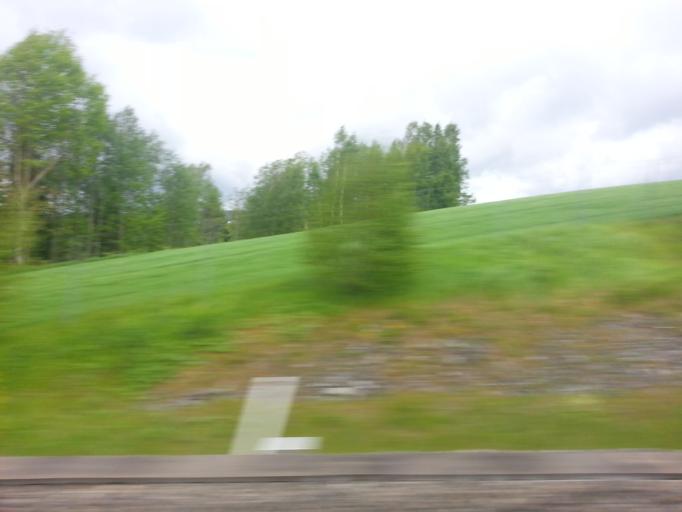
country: NO
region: Akershus
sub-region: Skedsmo
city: Leirsund
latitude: 60.0015
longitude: 11.0891
